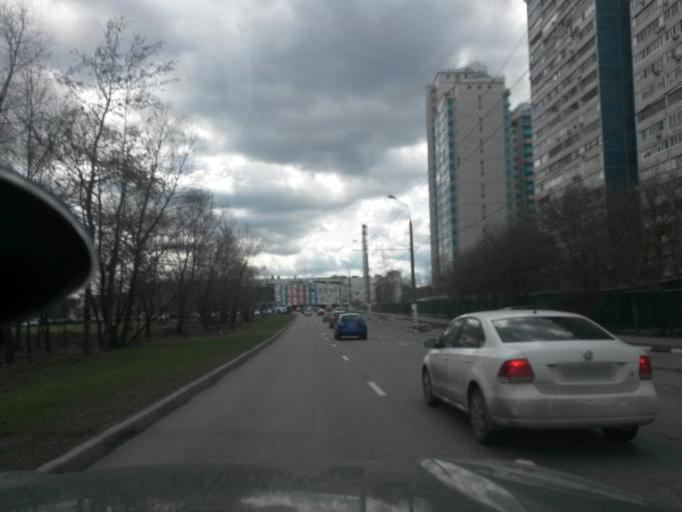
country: RU
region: Moscow
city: Yasenevo
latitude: 55.6003
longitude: 37.5284
